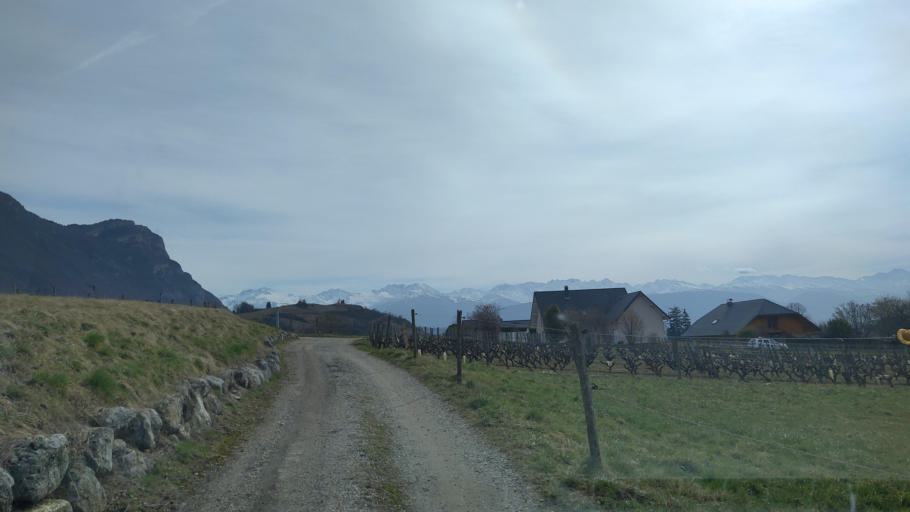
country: FR
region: Rhone-Alpes
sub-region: Departement de la Savoie
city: Challes-les-Eaux
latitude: 45.5351
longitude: 5.9881
